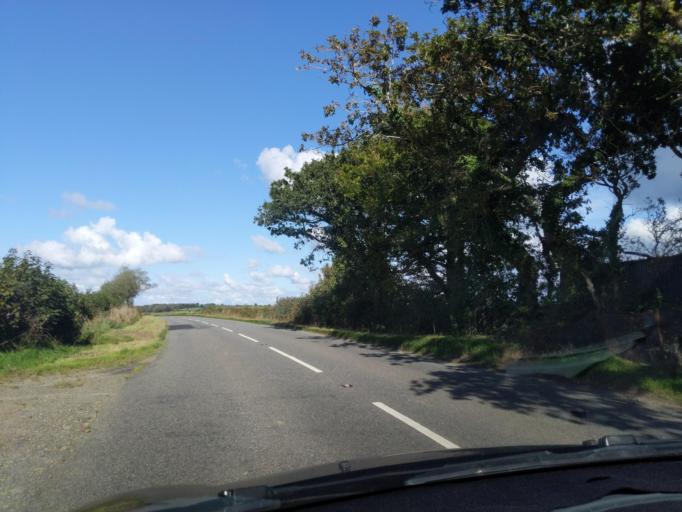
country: GB
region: England
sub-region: Cornwall
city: Boyton
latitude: 50.7372
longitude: -4.3232
